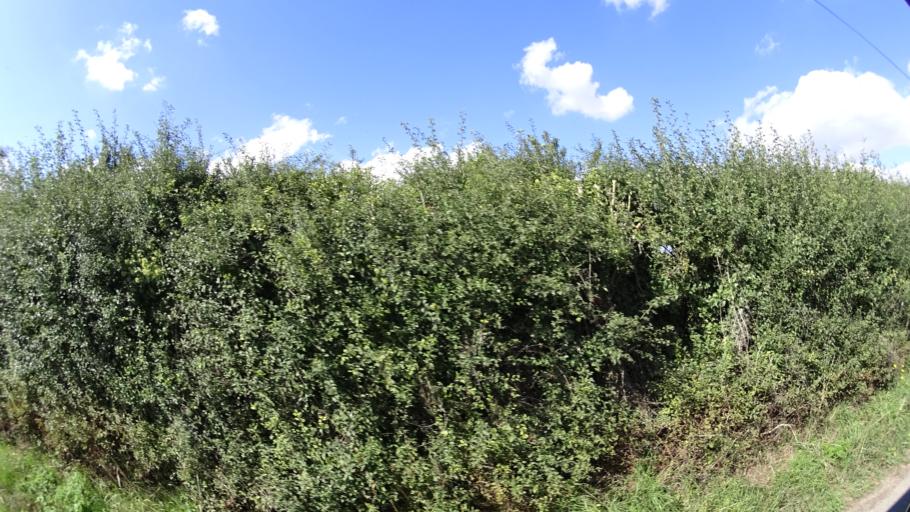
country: GB
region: England
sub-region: Hampshire
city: Abbotts Ann
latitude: 51.1675
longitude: -1.6038
